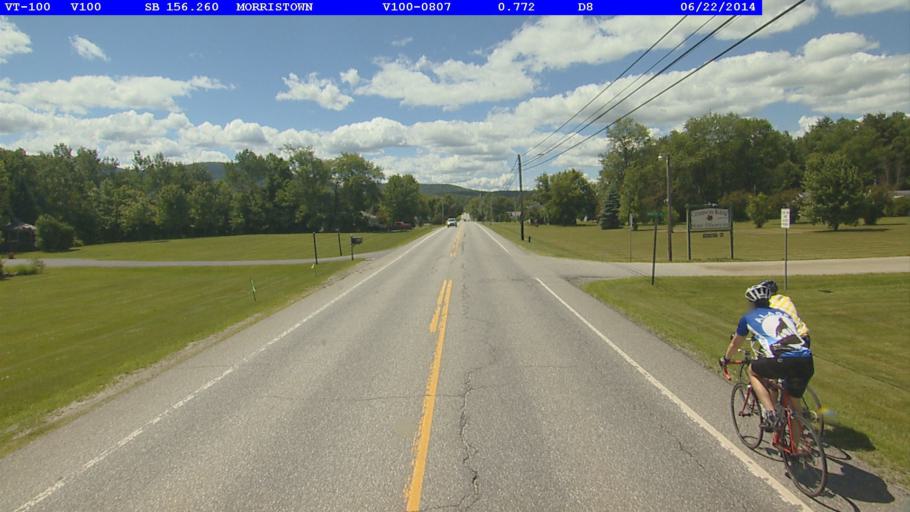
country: US
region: Vermont
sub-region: Lamoille County
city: Morristown
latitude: 44.5047
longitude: -72.6277
